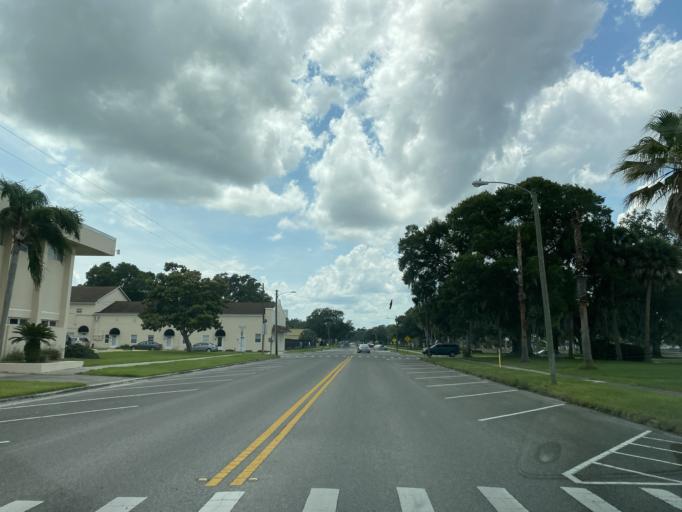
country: US
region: Florida
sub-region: Seminole County
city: Sanford
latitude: 28.8115
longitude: -81.2578
